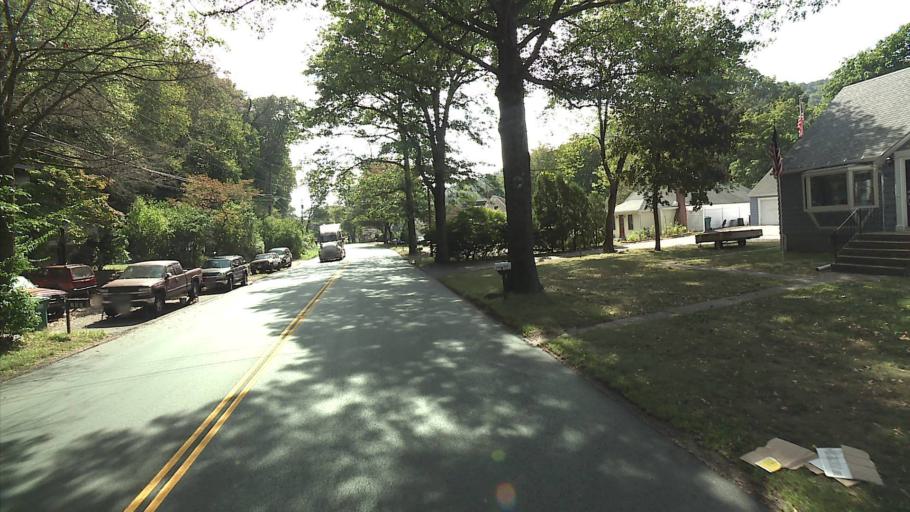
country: US
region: Connecticut
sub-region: Fairfield County
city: Shelton
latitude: 41.3552
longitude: -73.1365
